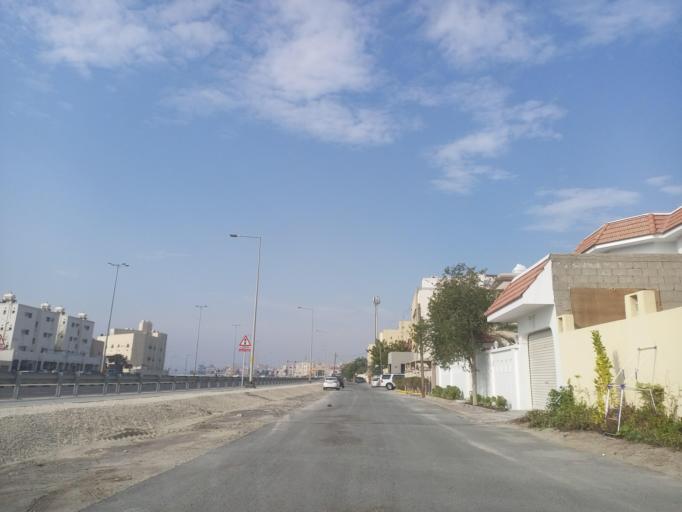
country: BH
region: Muharraq
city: Al Hadd
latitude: 26.2477
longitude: 50.6436
